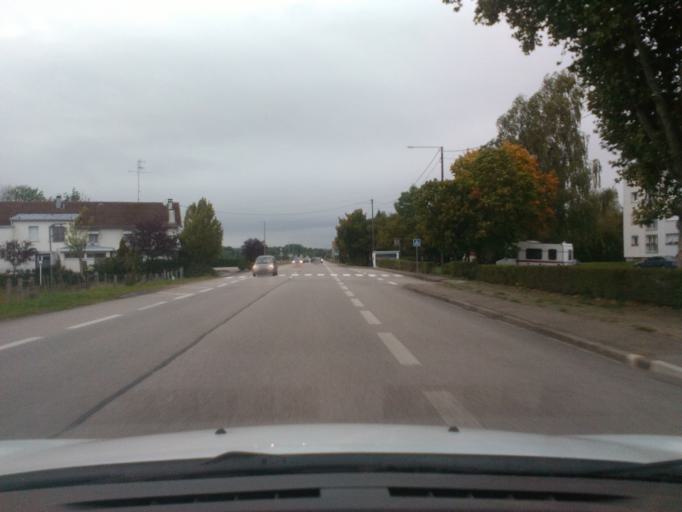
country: FR
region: Lorraine
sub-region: Departement des Vosges
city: Vincey
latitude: 48.3487
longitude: 6.3215
